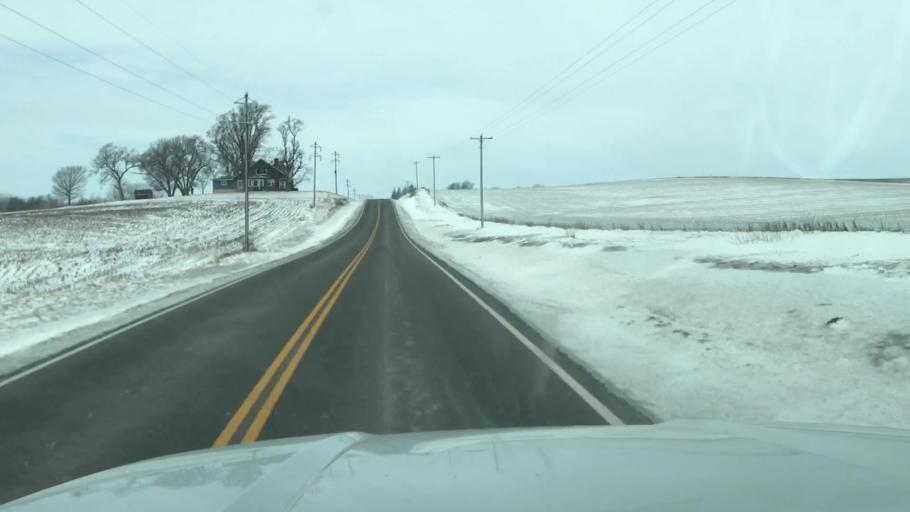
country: US
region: Missouri
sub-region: Holt County
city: Mound City
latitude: 40.1302
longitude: -95.1183
